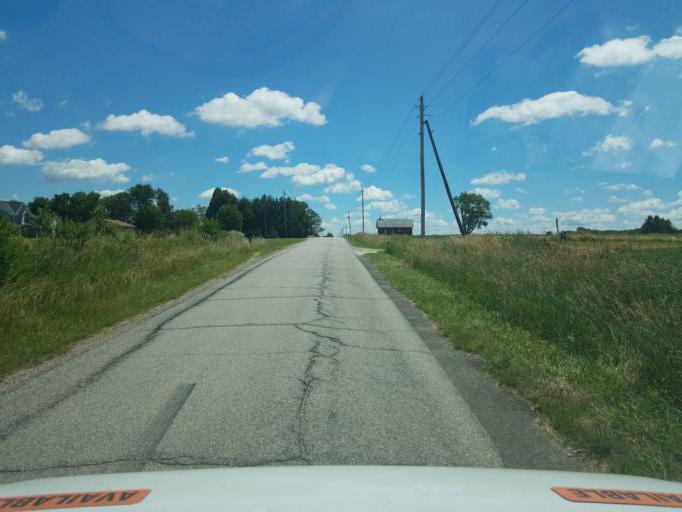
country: US
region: Ohio
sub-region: Crawford County
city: Bucyrus
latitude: 40.7403
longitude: -82.9080
